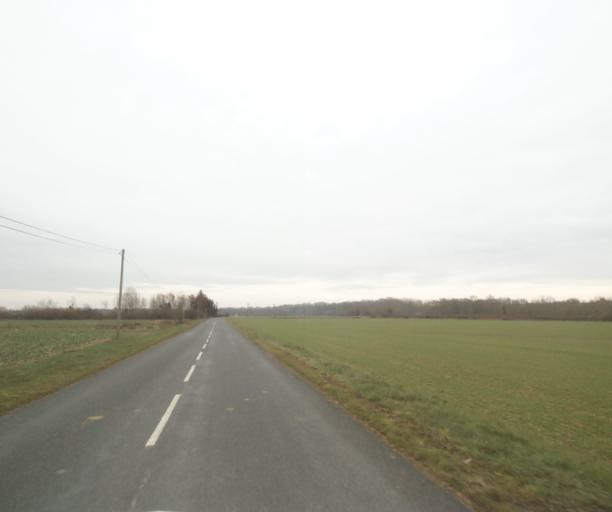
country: FR
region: Champagne-Ardenne
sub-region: Departement de la Haute-Marne
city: Villiers-en-Lieu
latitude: 48.6455
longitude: 4.7640
